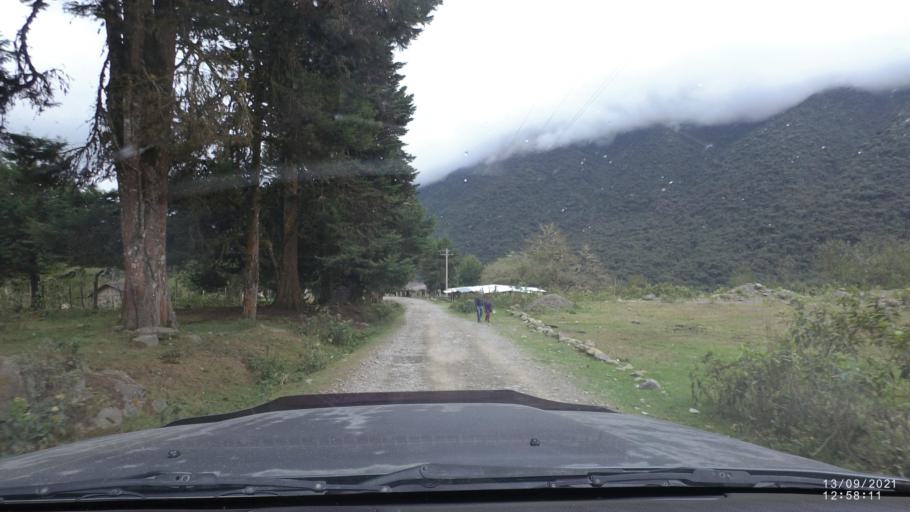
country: BO
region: Cochabamba
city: Colomi
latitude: -17.2382
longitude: -65.8171
